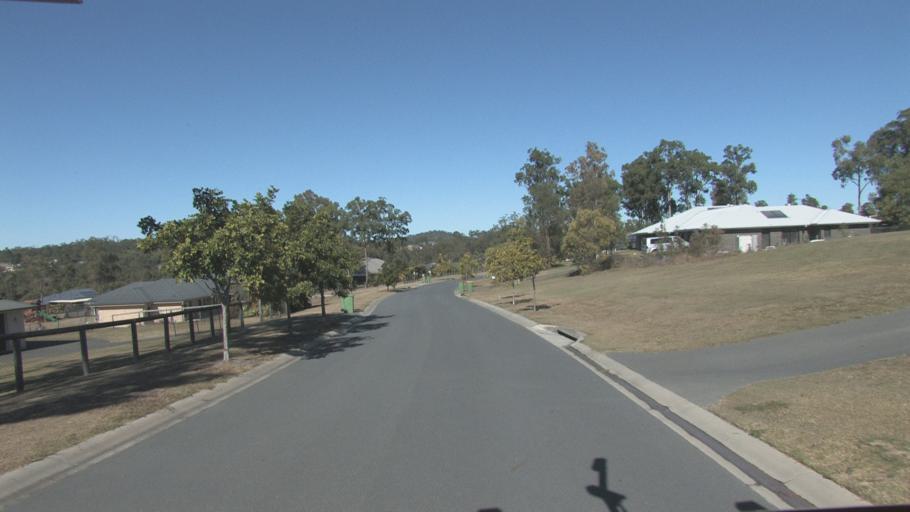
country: AU
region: Queensland
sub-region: Logan
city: North Maclean
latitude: -27.7514
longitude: 152.9500
